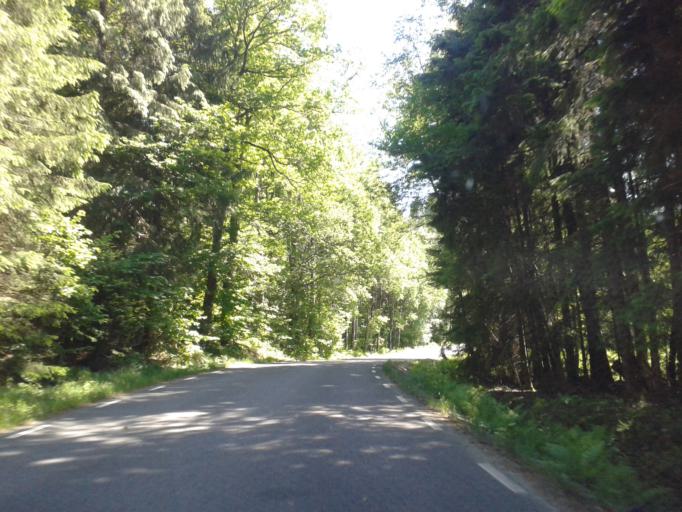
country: SE
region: Vaestra Goetaland
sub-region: Kungalvs Kommun
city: Diserod
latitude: 57.9702
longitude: 11.9893
